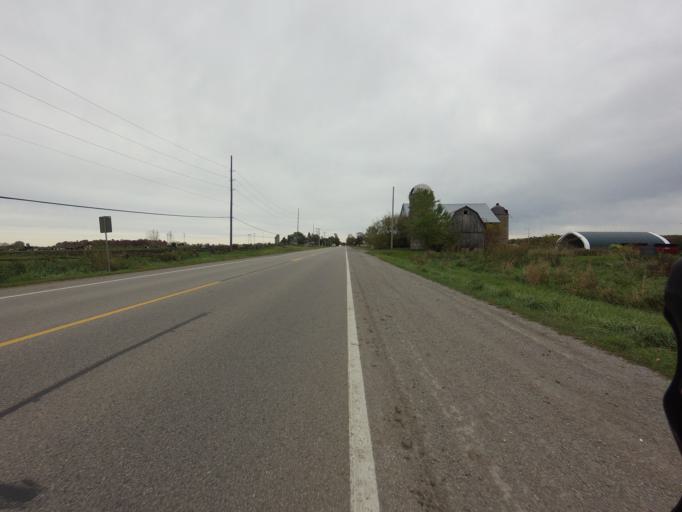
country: CA
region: Ontario
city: Brockville
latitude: 44.6301
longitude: -75.9417
